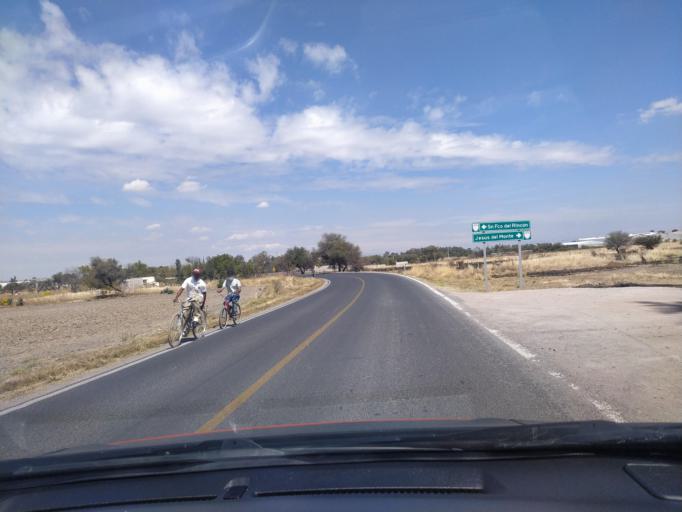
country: MX
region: Guanajuato
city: San Roque
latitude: 20.9712
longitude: -101.8437
